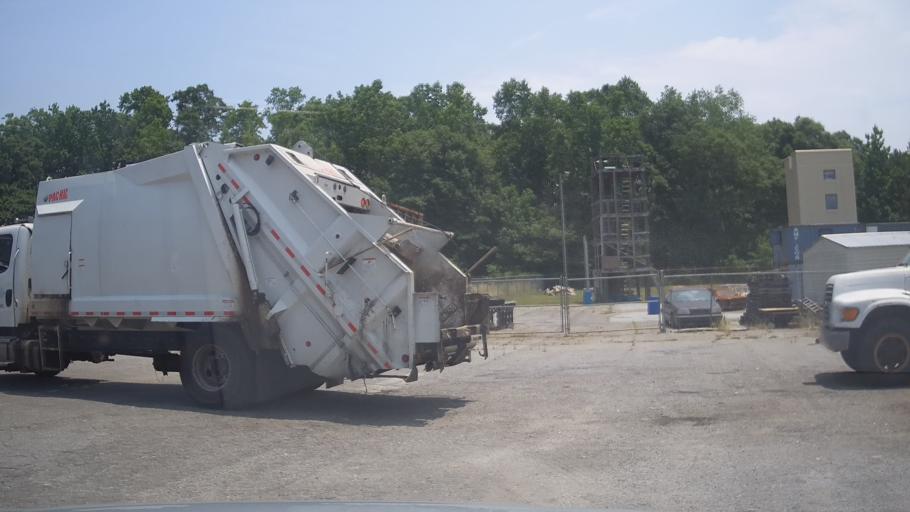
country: US
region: Georgia
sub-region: Hart County
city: Hartwell
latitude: 34.3468
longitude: -82.9180
